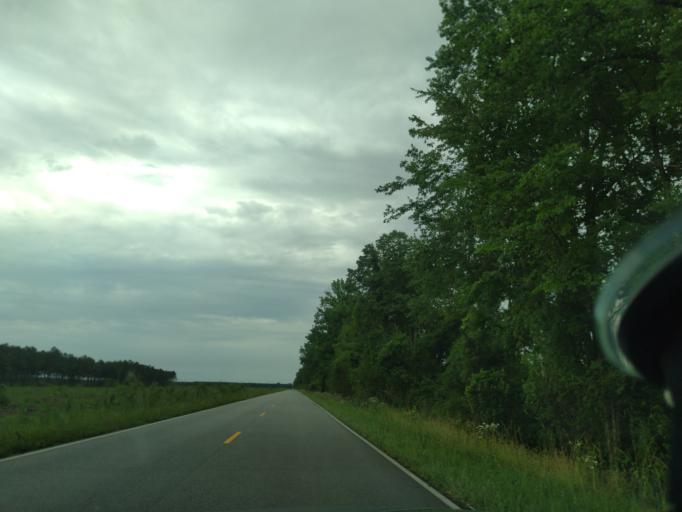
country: US
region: North Carolina
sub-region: Washington County
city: Plymouth
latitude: 35.8688
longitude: -76.5906
